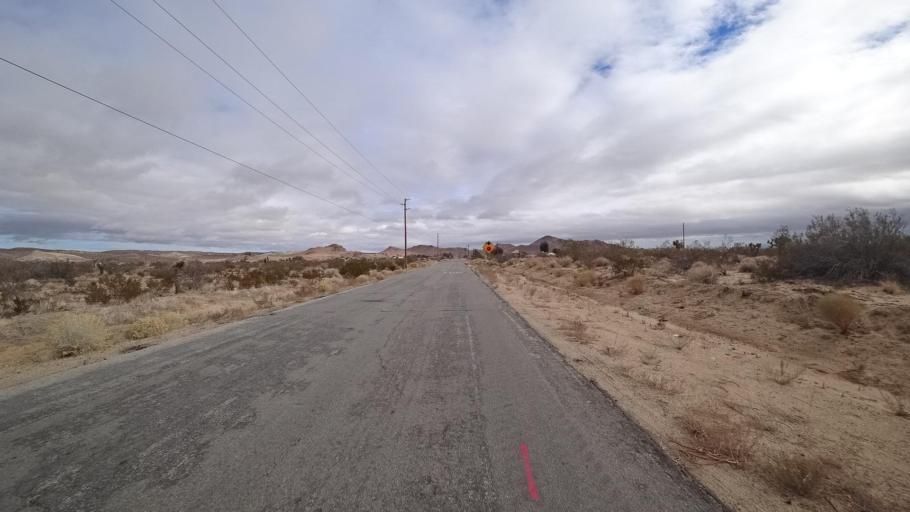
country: US
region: California
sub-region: Kern County
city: Rosamond
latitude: 34.8927
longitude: -118.2231
